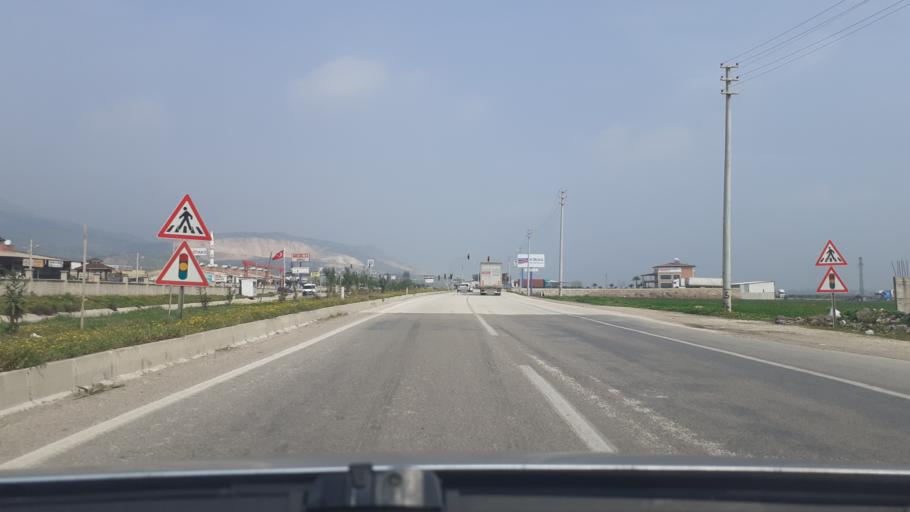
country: TR
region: Hatay
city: Kirikhan
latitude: 36.5220
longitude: 36.3769
